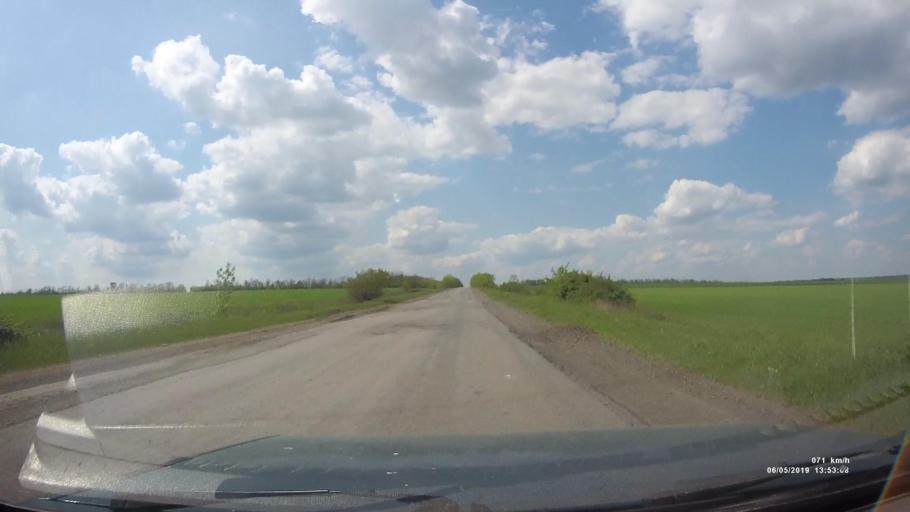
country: RU
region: Rostov
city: Melikhovskaya
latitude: 47.6655
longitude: 40.4690
